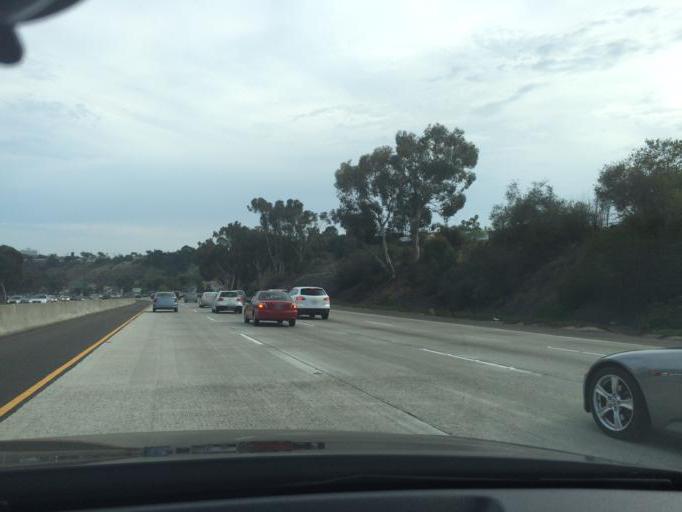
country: US
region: California
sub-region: San Diego County
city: San Diego
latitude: 32.7829
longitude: -117.1622
